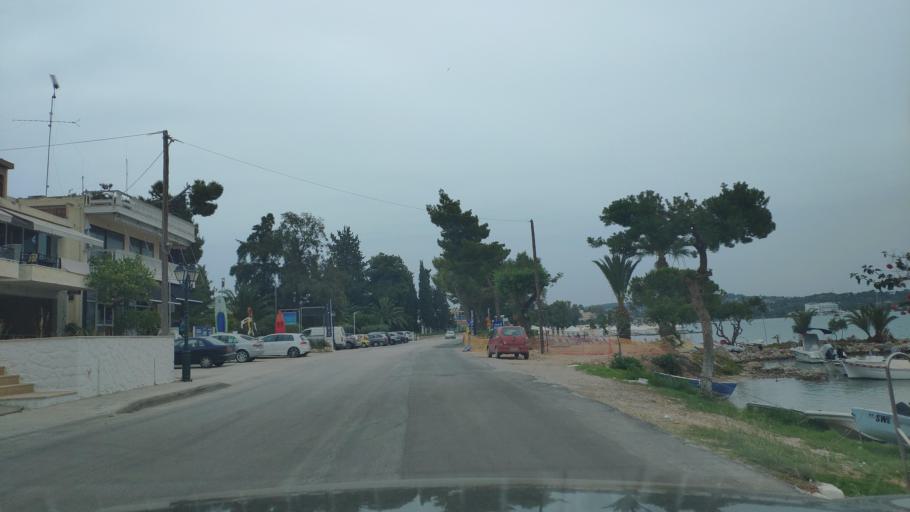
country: GR
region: Peloponnese
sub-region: Nomos Argolidos
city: Porto Cheli
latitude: 37.3275
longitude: 23.1503
